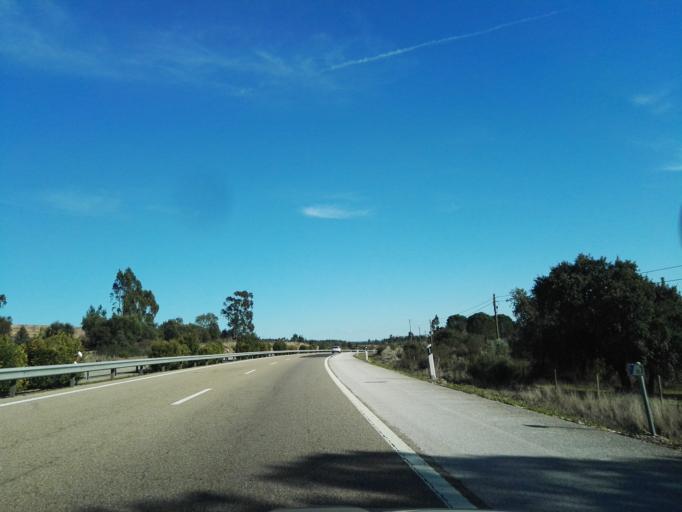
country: PT
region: Santarem
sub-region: Constancia
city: Constancia
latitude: 39.4920
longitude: -8.2989
